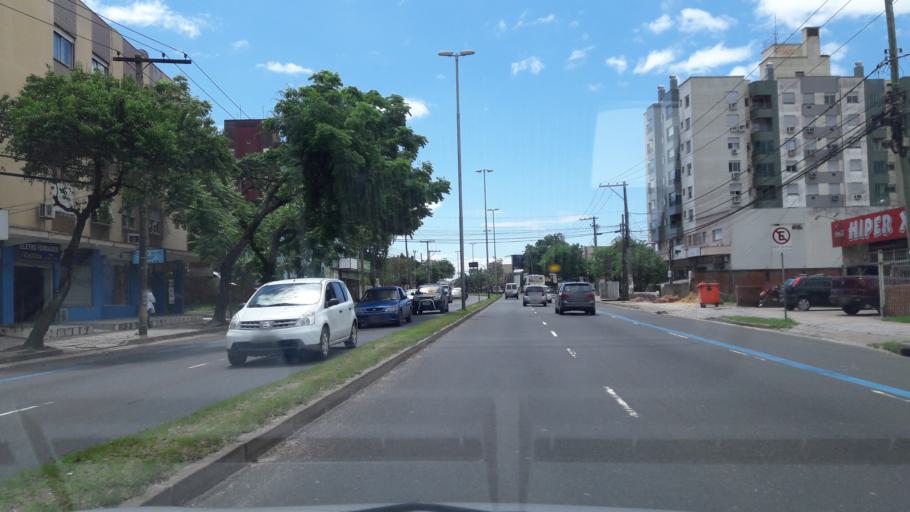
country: BR
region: Rio Grande do Sul
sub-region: Porto Alegre
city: Porto Alegre
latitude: -30.1050
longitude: -51.2298
